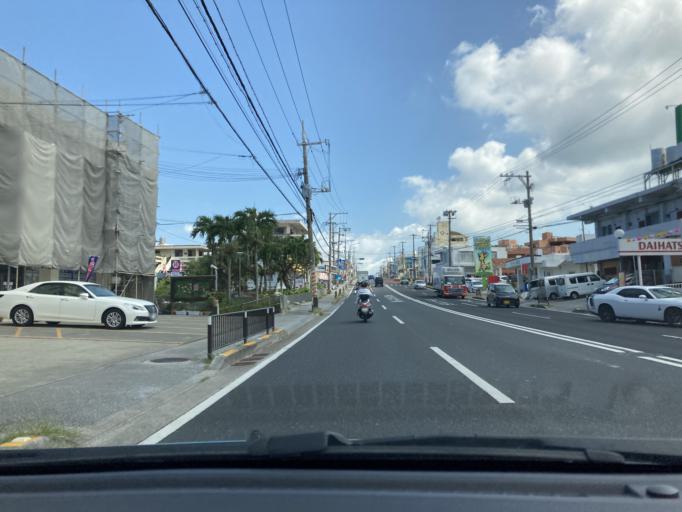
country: JP
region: Okinawa
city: Ginowan
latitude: 26.2651
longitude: 127.7639
